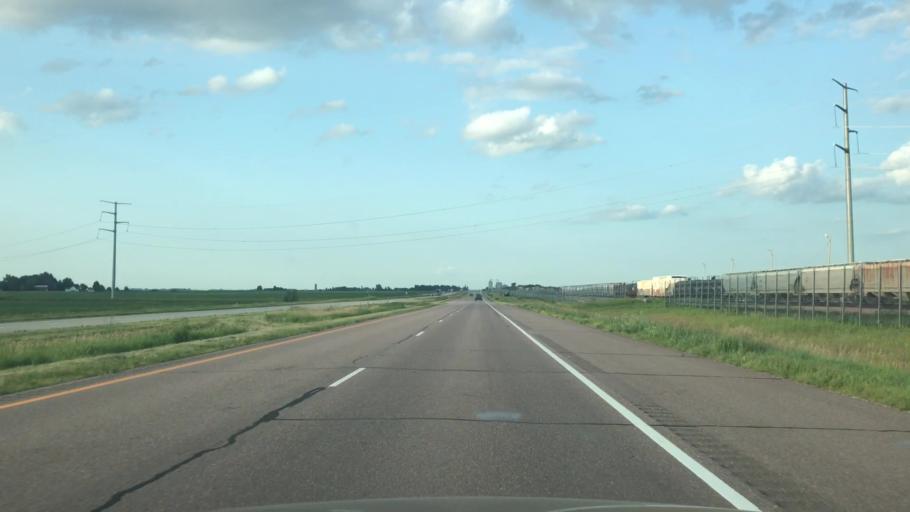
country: US
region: Minnesota
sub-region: Nobles County
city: Worthington
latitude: 43.6702
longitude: -95.5152
